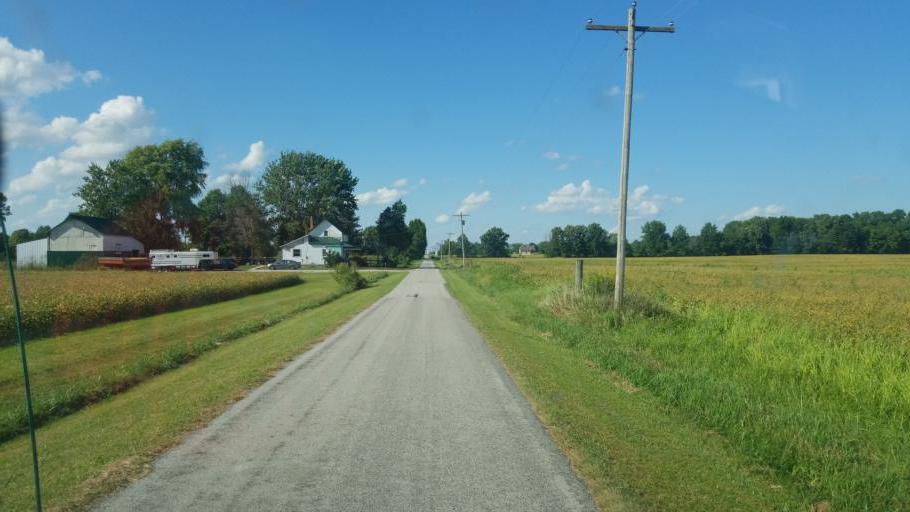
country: US
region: Ohio
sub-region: Marion County
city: Marion
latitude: 40.6256
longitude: -83.2694
